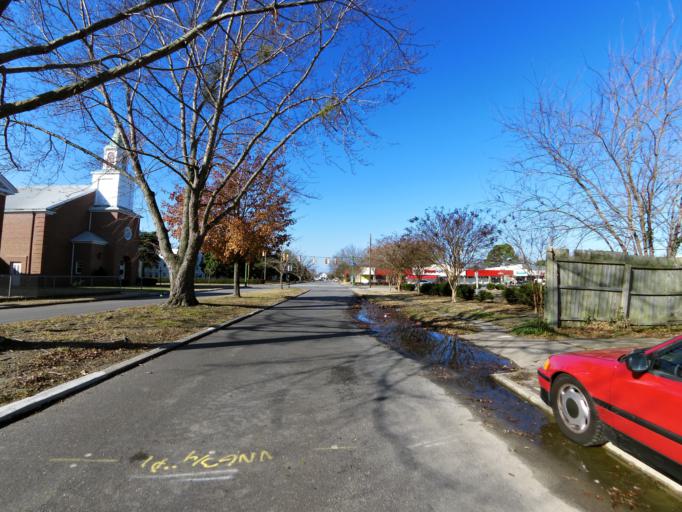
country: US
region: Virginia
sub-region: City of Hampton
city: Hampton
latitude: 37.0017
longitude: -76.3791
